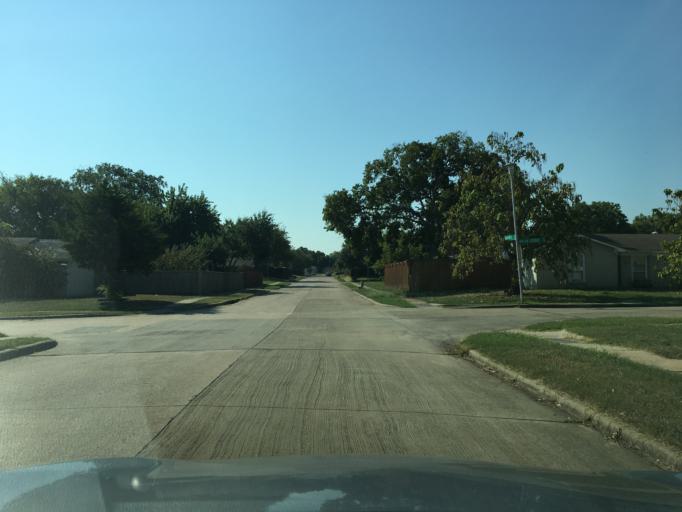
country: US
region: Texas
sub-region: Dallas County
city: Garland
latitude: 32.9416
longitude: -96.6528
